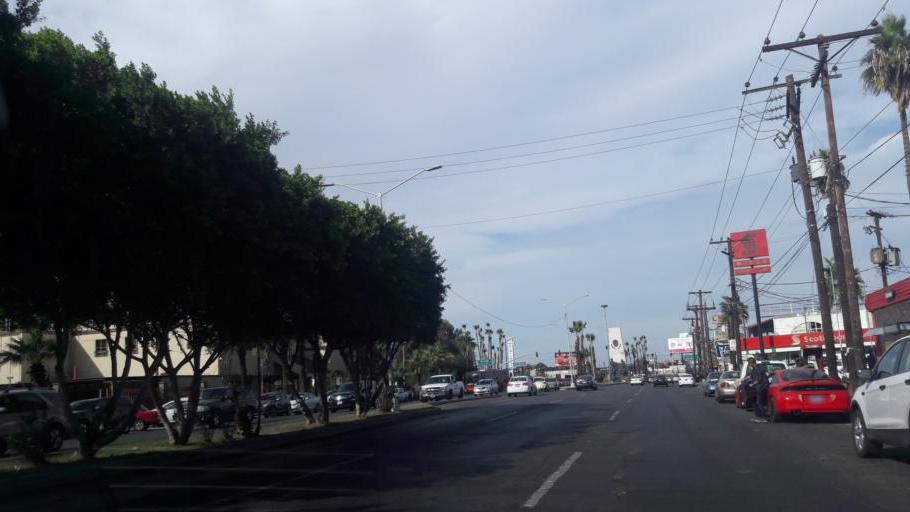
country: MX
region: Baja California
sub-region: Mexicali
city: Mexicali
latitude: 32.6457
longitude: -115.4515
